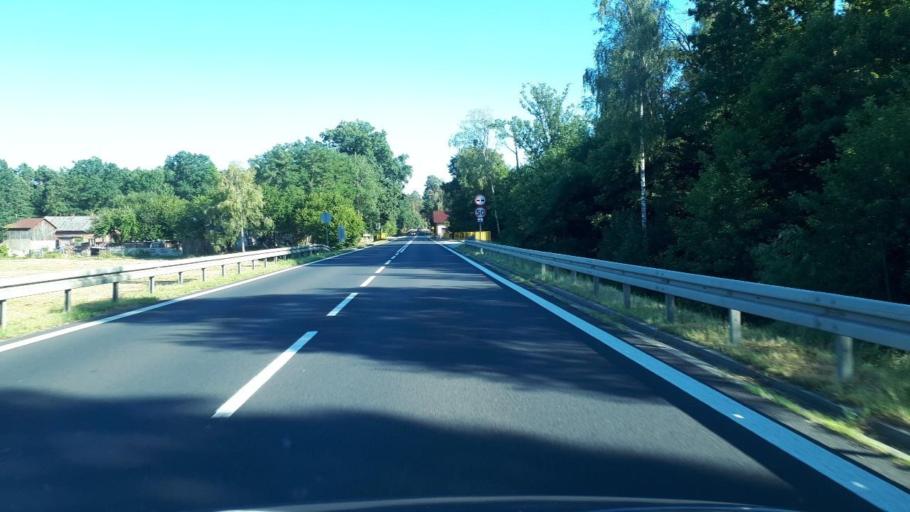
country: PL
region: Silesian Voivodeship
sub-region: Powiat tarnogorski
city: Tworog
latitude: 50.5874
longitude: 18.7039
